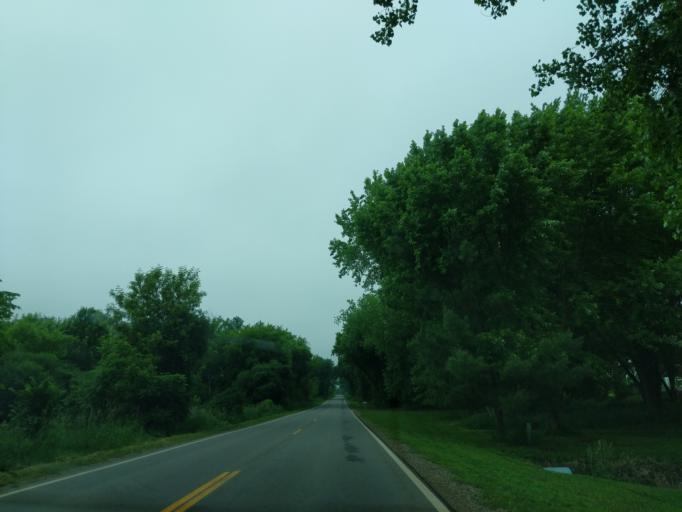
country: US
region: Michigan
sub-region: Jackson County
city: Spring Arbor
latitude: 42.2120
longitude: -84.5702
